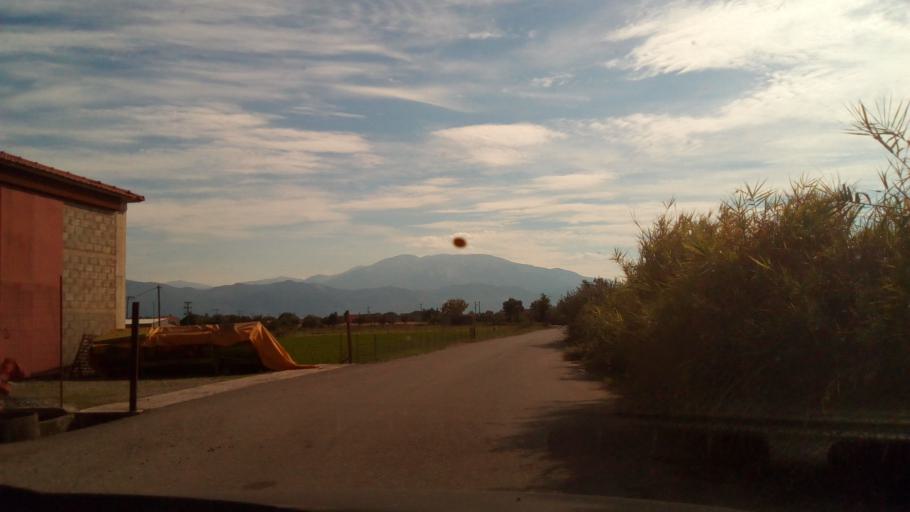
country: GR
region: West Greece
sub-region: Nomos Aitolias kai Akarnanias
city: Nafpaktos
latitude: 38.4085
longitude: 21.8966
